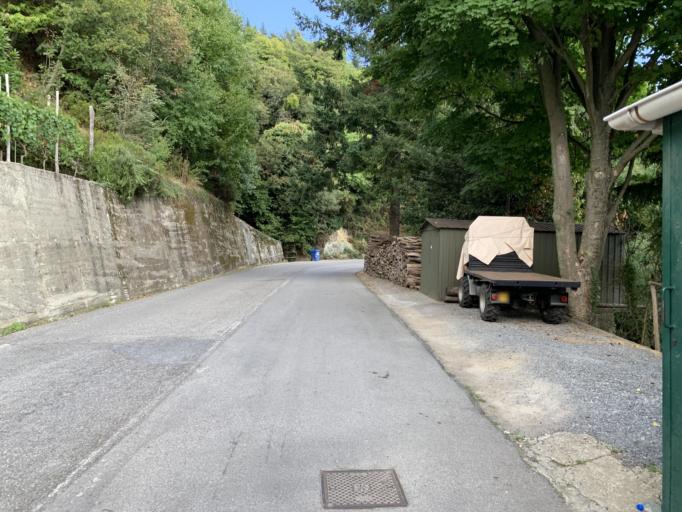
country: IT
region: Liguria
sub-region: Provincia di Savona
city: Orco Feglino
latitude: 44.2216
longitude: 8.3064
